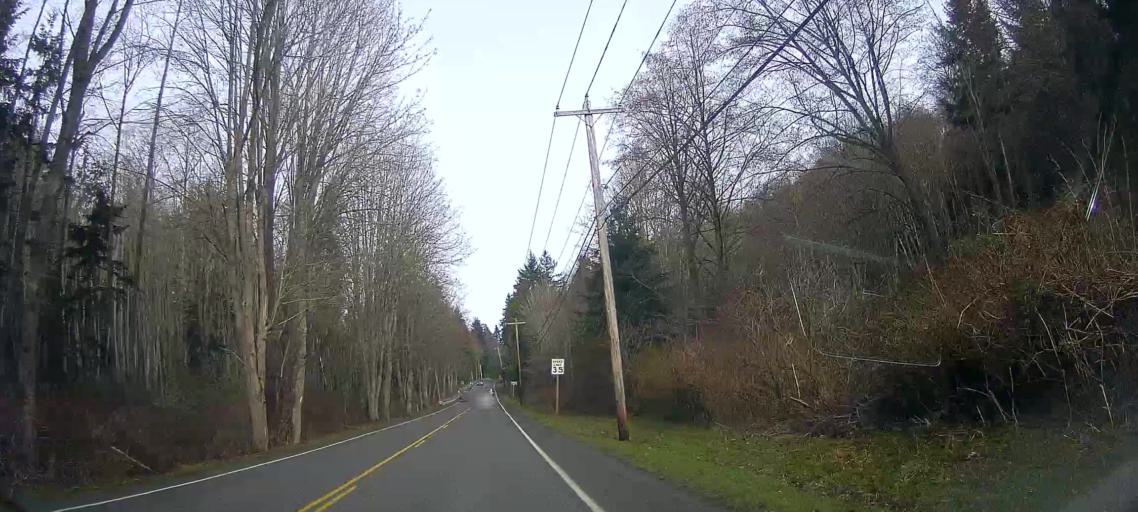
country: US
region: Washington
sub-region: Island County
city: Camano
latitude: 48.2501
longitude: -122.5121
